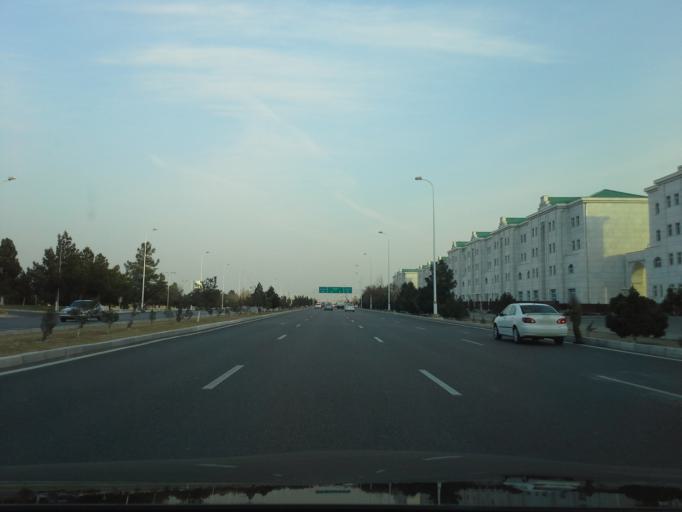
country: TM
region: Ahal
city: Ashgabat
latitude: 37.9883
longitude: 58.3229
